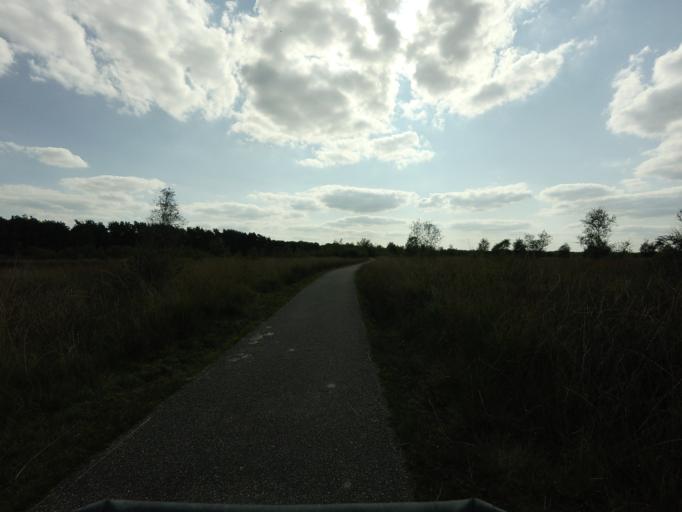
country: NL
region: Drenthe
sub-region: Gemeente Hoogeveen
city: Hoogeveen
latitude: 52.7987
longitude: 6.4446
